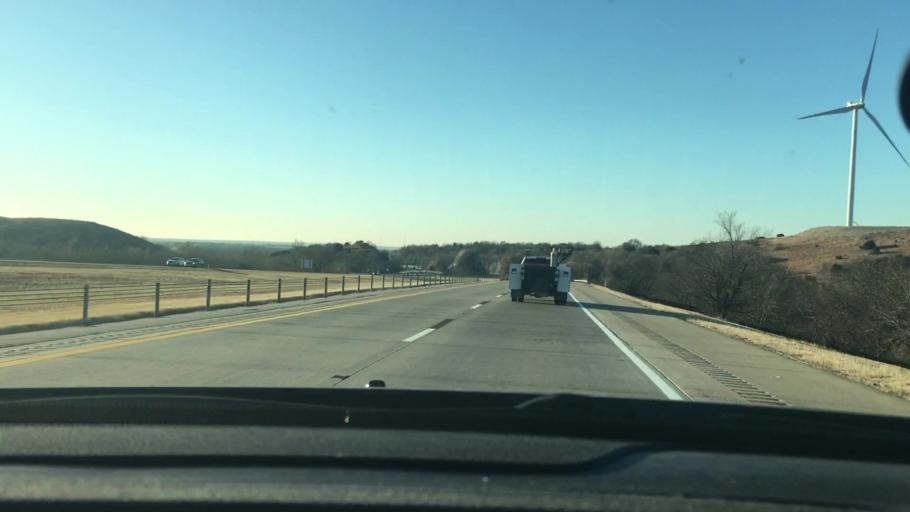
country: US
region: Oklahoma
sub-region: Murray County
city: Davis
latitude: 34.3628
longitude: -97.1479
